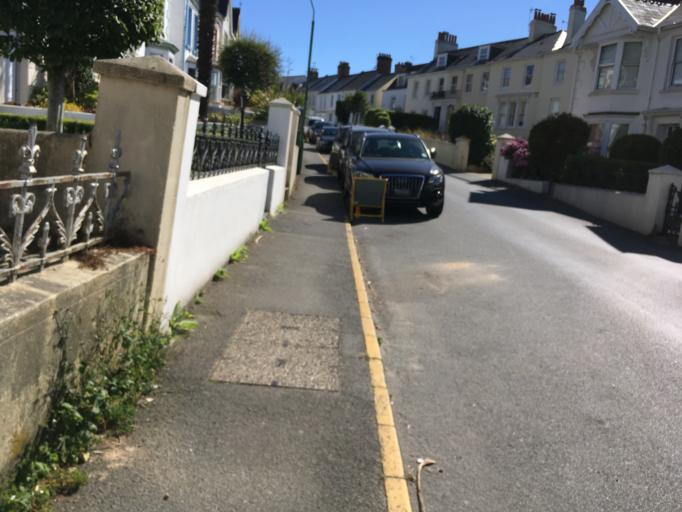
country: GG
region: St Peter Port
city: Saint Peter Port
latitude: 49.4576
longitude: -2.5468
